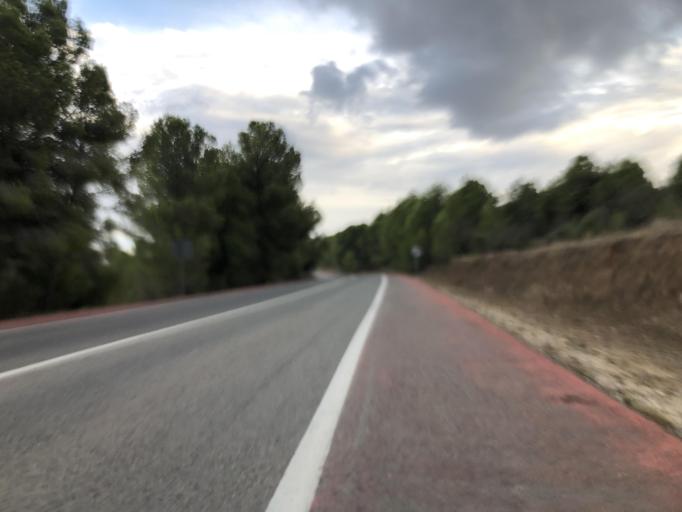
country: ES
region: Valencia
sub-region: Provincia de Alicante
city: Polop
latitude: 38.6339
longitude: -0.1520
